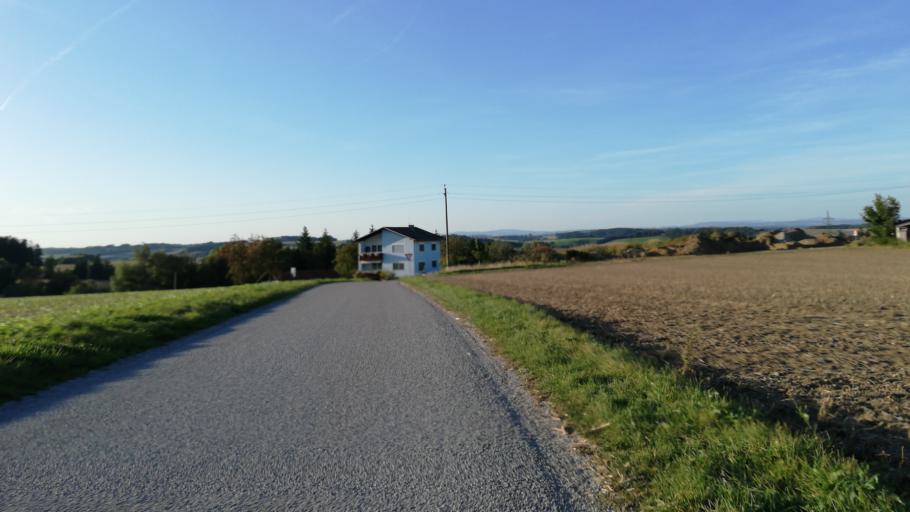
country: AT
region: Upper Austria
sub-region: Wels-Land
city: Offenhausen
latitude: 48.1640
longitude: 13.8587
